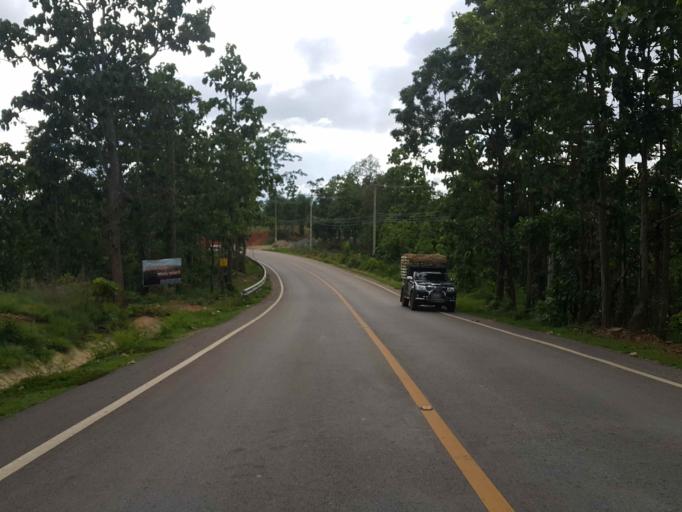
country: TH
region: Chiang Mai
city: Mae Chaem
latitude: 18.5018
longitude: 98.3980
